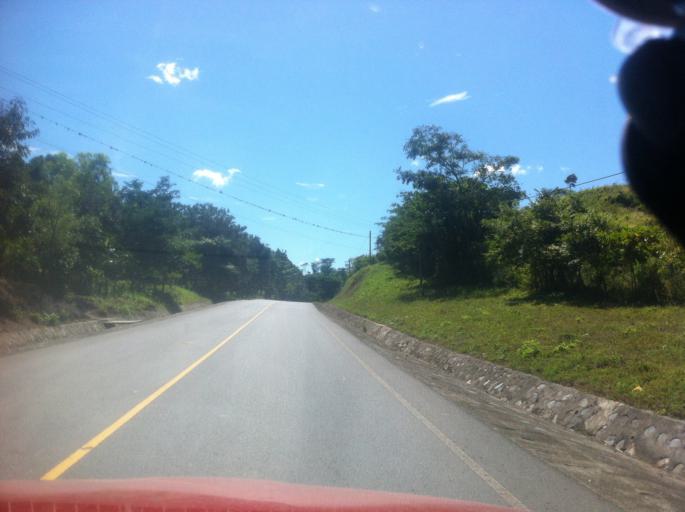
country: NI
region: Matagalpa
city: San Ramon
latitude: 12.9054
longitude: -85.8440
